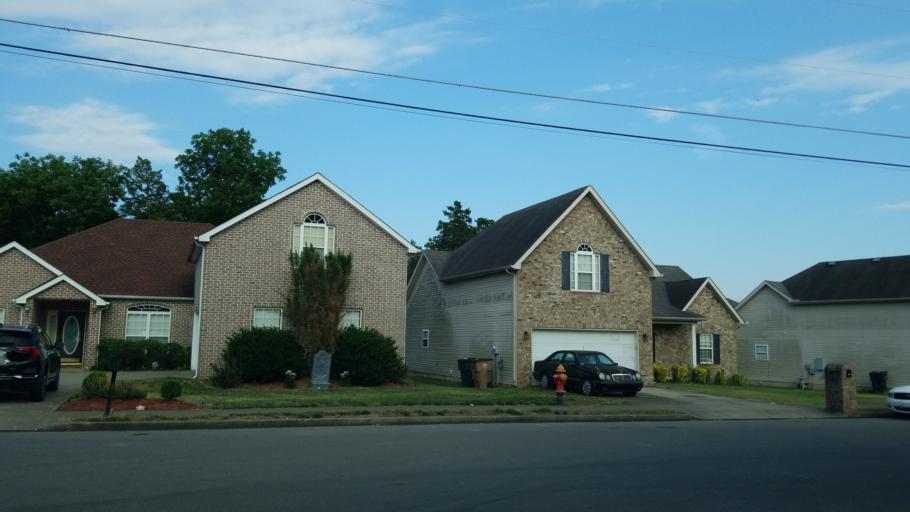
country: US
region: Tennessee
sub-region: Rutherford County
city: La Vergne
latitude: 36.0347
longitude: -86.5863
